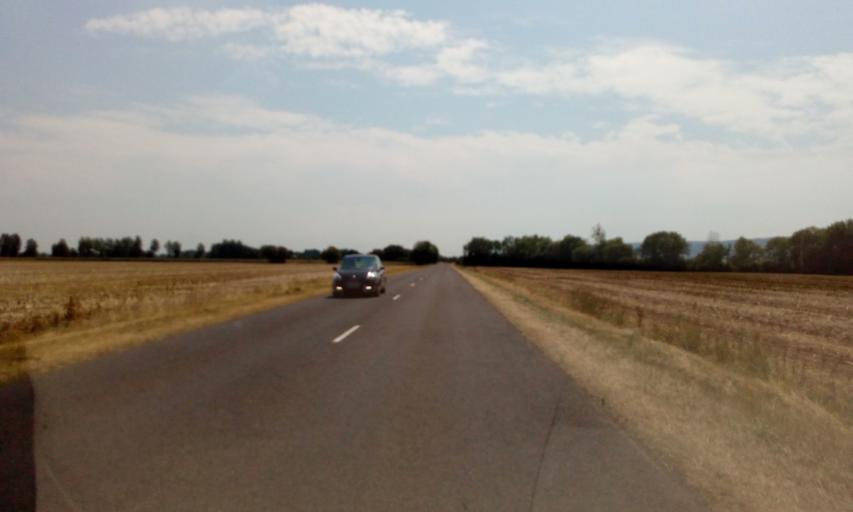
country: FR
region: Lorraine
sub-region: Departement de la Meuse
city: Etain
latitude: 49.0876
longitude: 5.6310
